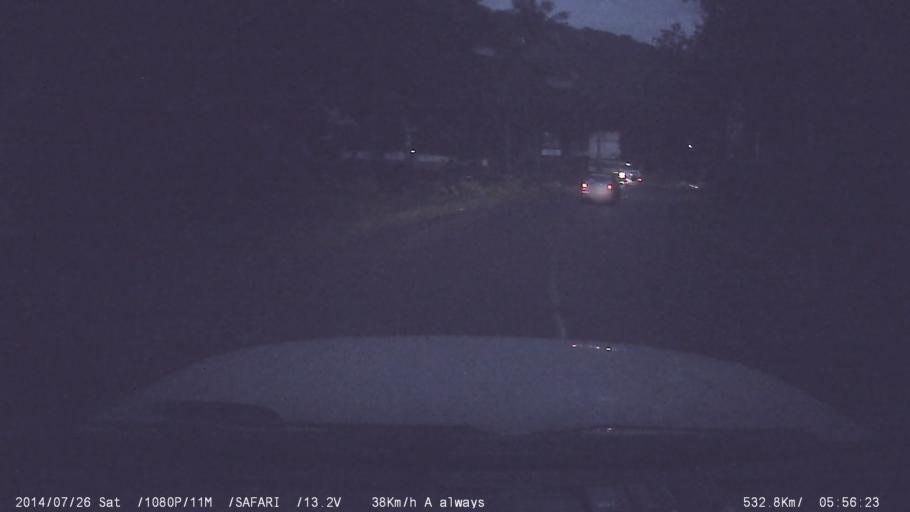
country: IN
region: Kerala
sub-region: Ernakulam
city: Muvattupuzha
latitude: 9.9336
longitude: 76.5744
